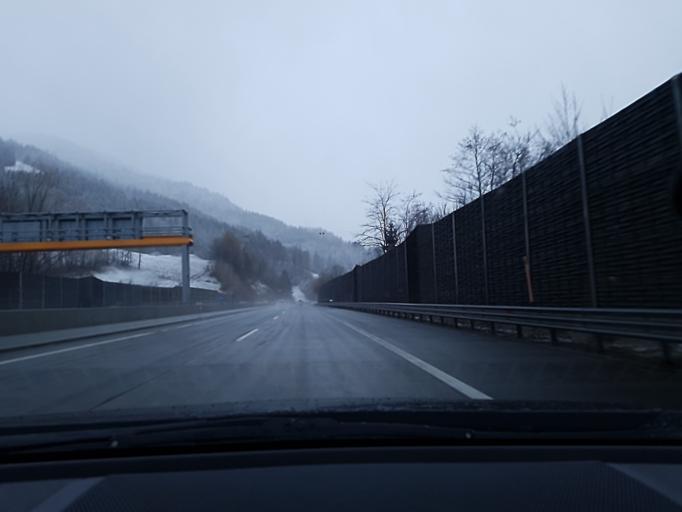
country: AT
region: Salzburg
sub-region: Politischer Bezirk Hallein
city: Kuchl
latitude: 47.6112
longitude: 13.1429
